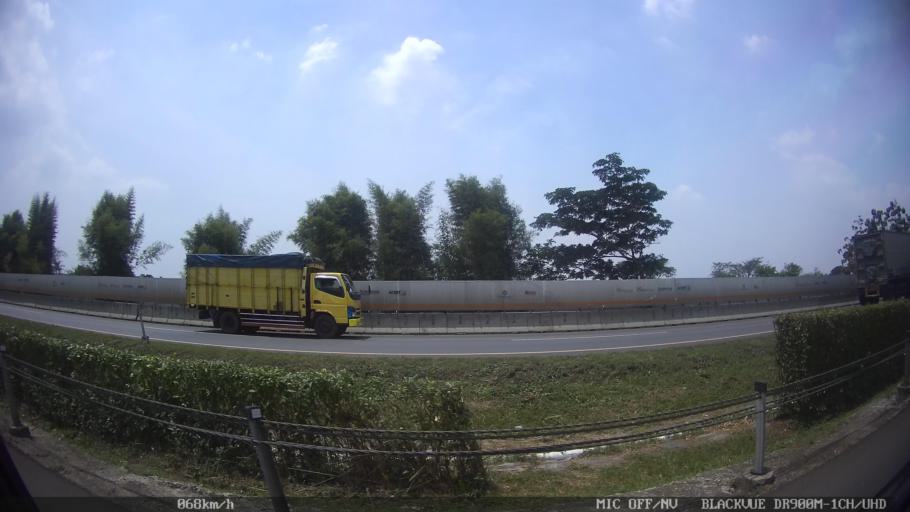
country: ID
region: Banten
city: Serang
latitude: -6.1357
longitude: 106.2139
